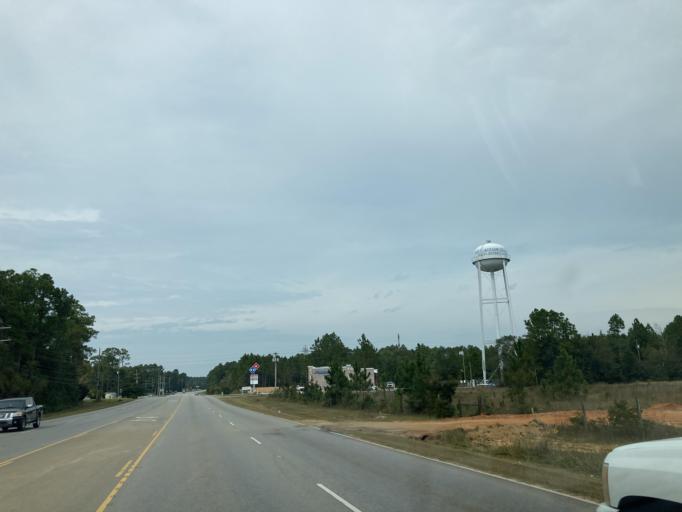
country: US
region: Mississippi
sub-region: Jackson County
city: Gulf Hills
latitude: 30.4600
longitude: -88.8442
